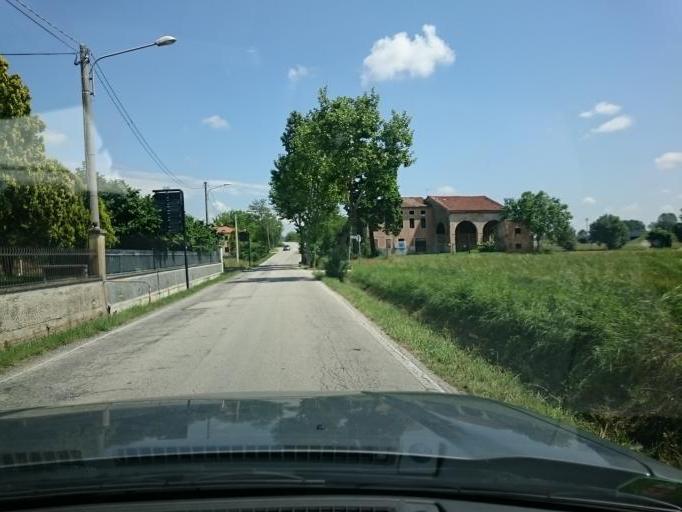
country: IT
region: Veneto
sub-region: Provincia di Vicenza
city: Torri di Quartesolo
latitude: 45.5104
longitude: 11.5964
